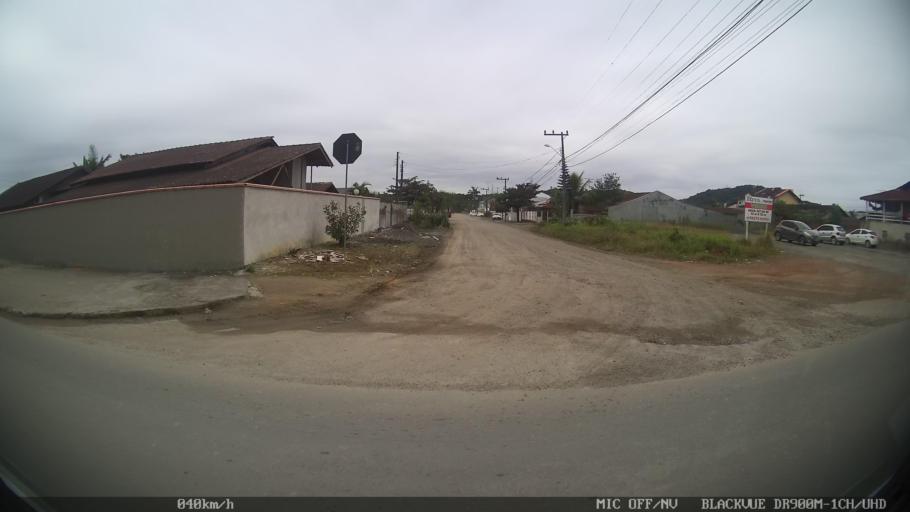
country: BR
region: Santa Catarina
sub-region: Joinville
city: Joinville
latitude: -26.2938
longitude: -48.9000
